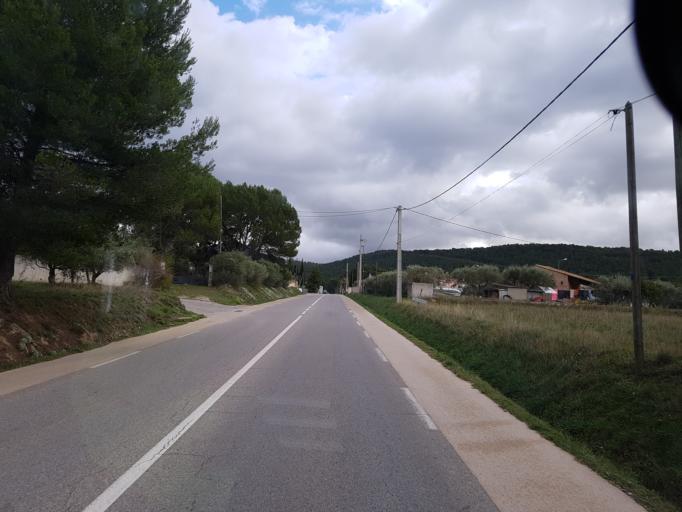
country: FR
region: Provence-Alpes-Cote d'Azur
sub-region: Departement des Bouches-du-Rhone
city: Cuges-les-Pins
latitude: 43.2757
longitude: 5.7107
